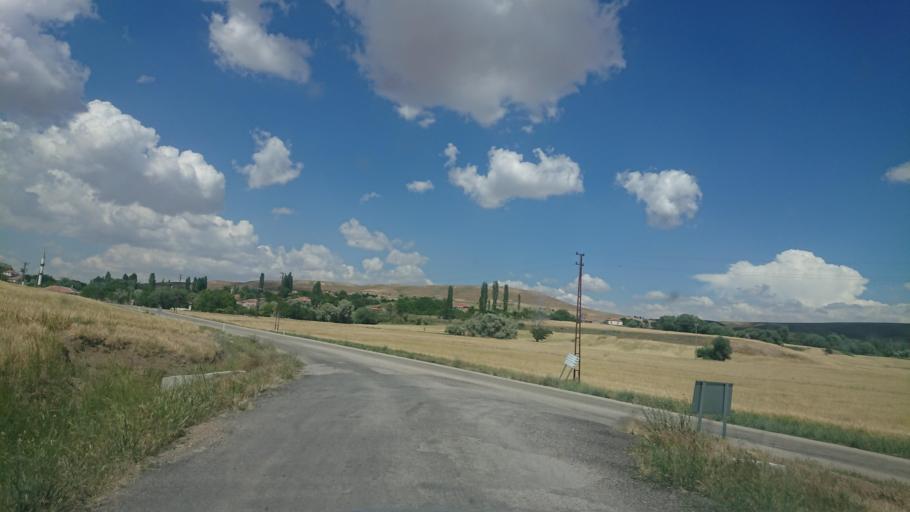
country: TR
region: Aksaray
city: Agacoren
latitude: 38.8000
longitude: 33.8246
